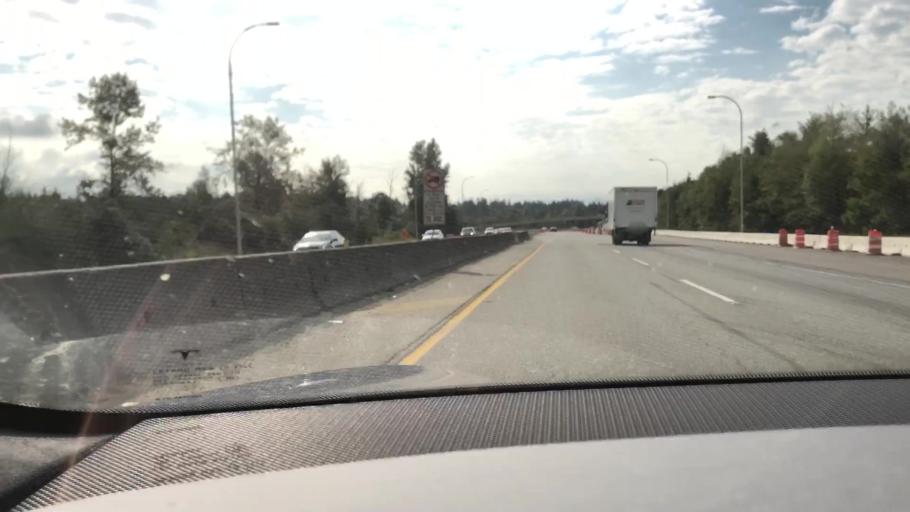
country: CA
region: British Columbia
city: Delta
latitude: 49.1375
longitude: -122.9319
